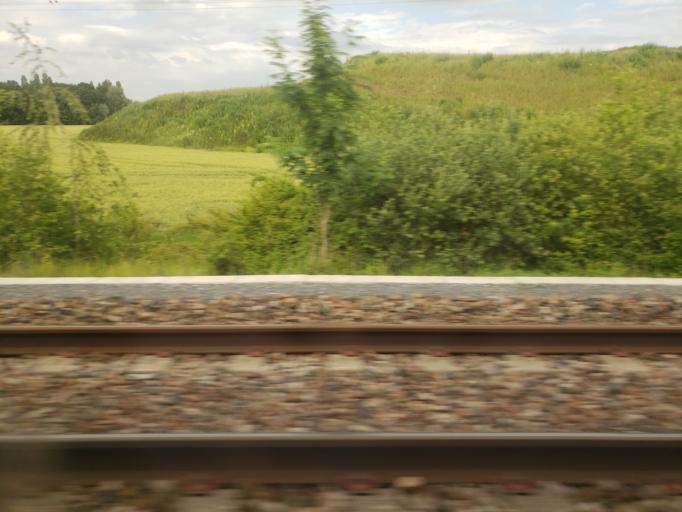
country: FR
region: Ile-de-France
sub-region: Departement de Seine-et-Marne
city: Serris
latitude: 48.8214
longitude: 2.7816
